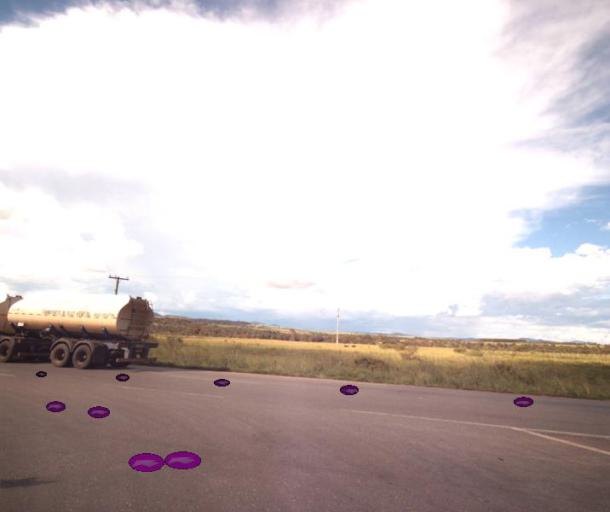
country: BR
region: Goias
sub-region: Rialma
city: Rialma
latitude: -15.4474
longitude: -49.5058
